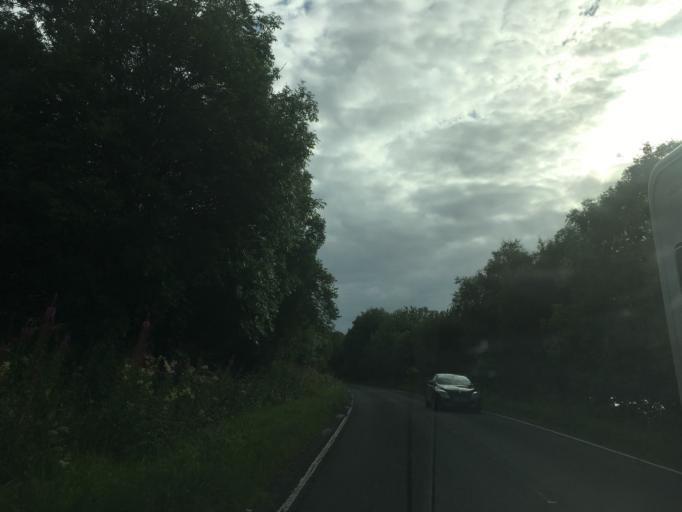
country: GB
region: Scotland
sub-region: Argyll and Bute
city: Oban
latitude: 56.3605
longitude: -5.4527
